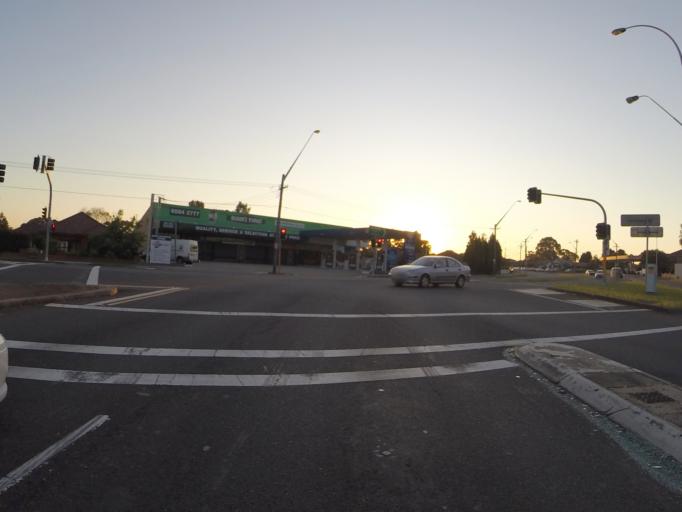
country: AU
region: New South Wales
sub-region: Hurstville
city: Penshurst
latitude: -33.9581
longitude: 151.0695
